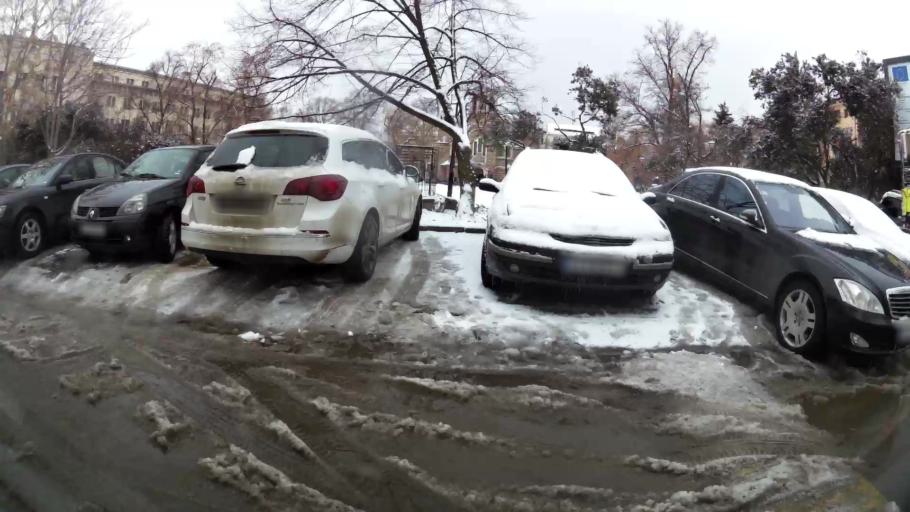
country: BG
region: Sofia-Capital
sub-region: Stolichna Obshtina
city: Sofia
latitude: 42.6905
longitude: 23.3266
